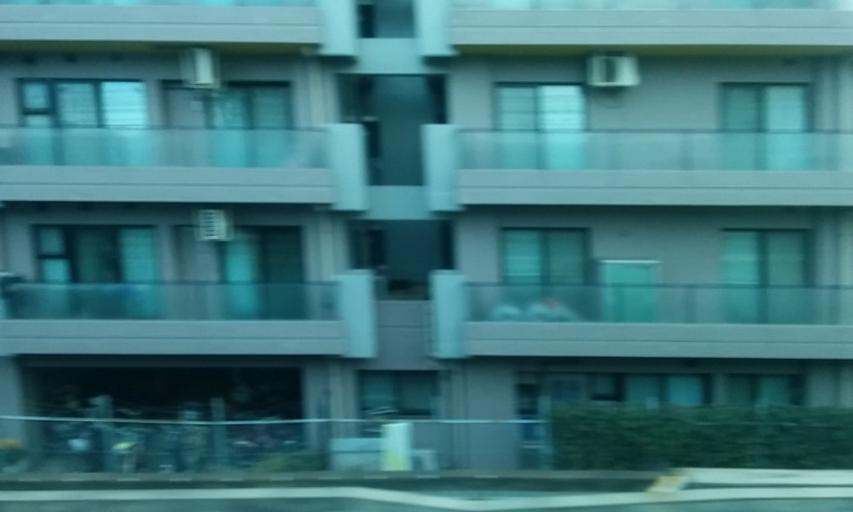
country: JP
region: Saitama
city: Kawaguchi
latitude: 35.7973
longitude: 139.7183
